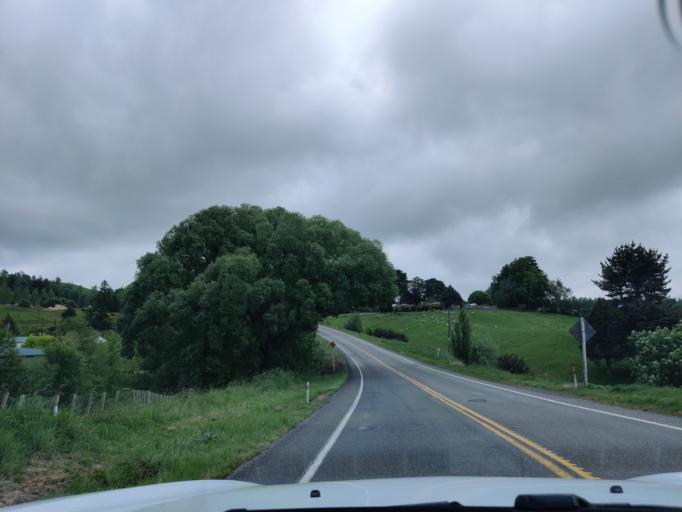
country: NZ
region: Manawatu-Wanganui
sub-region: Ruapehu District
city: Waiouru
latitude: -39.6572
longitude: 175.7793
